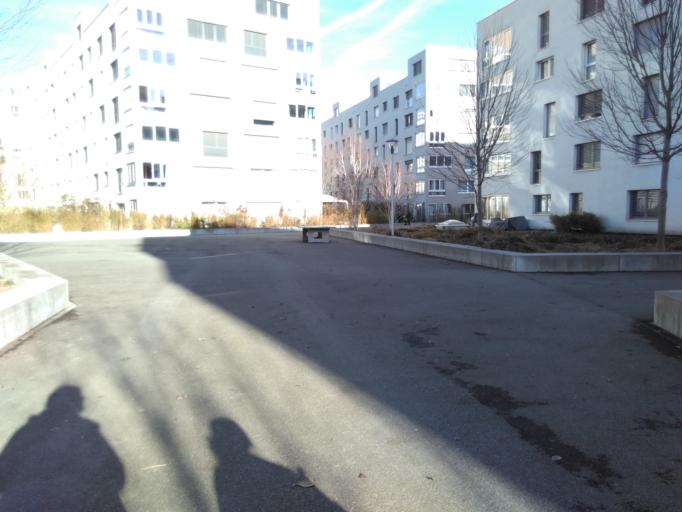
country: CH
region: Zurich
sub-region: Bezirk Buelach
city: Glattbrugg / Wydacker/Bettacker/Laettenwiesen
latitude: 47.4234
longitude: 8.5652
